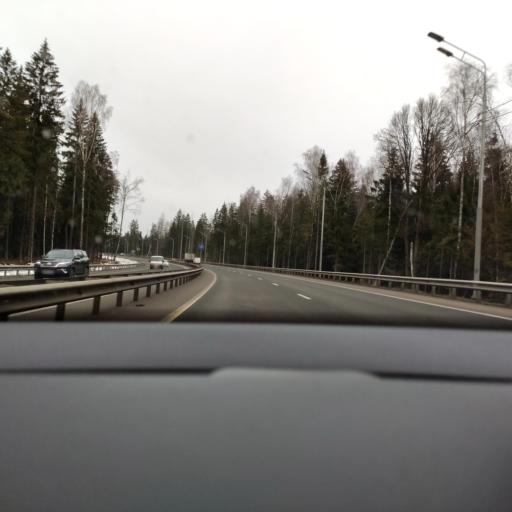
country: RU
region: Moskovskaya
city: Bol'shiye Vyazemy
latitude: 55.6529
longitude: 36.9871
